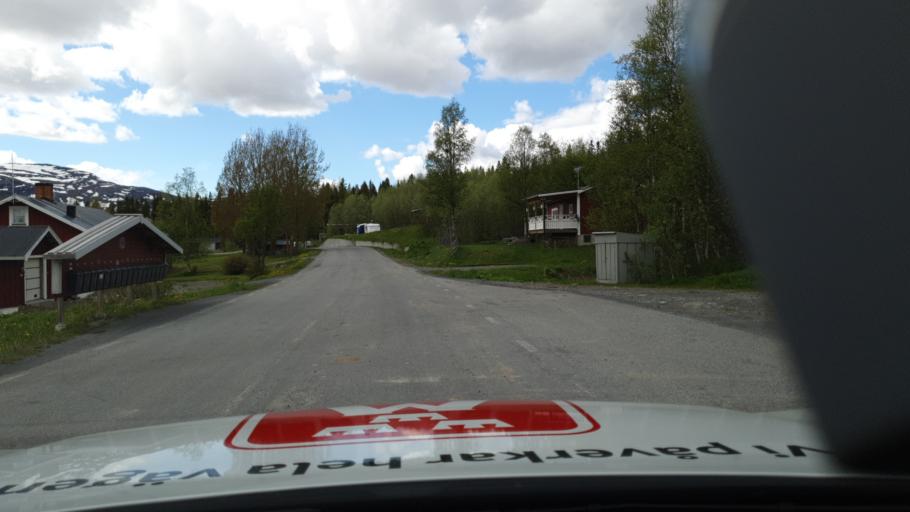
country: SE
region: Jaemtland
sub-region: Are Kommun
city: Are
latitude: 63.2170
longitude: 13.0452
